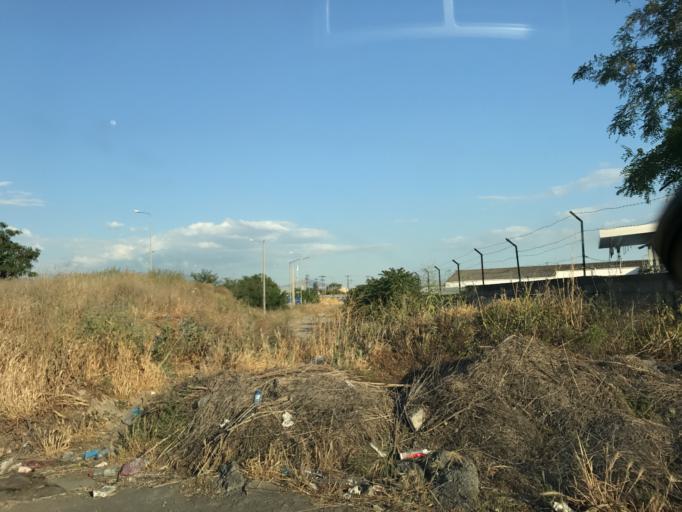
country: GR
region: Central Macedonia
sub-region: Nomos Thessalonikis
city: Menemeni
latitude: 40.6520
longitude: 22.9001
